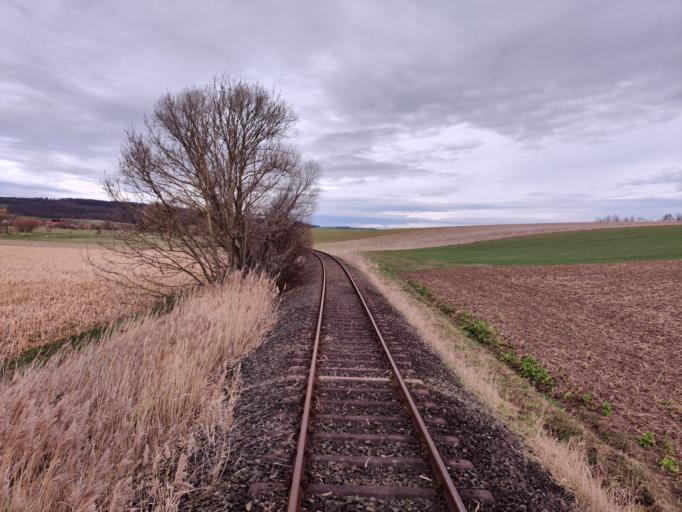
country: DE
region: Lower Saxony
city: Bockenem
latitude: 52.0283
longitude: 10.1247
